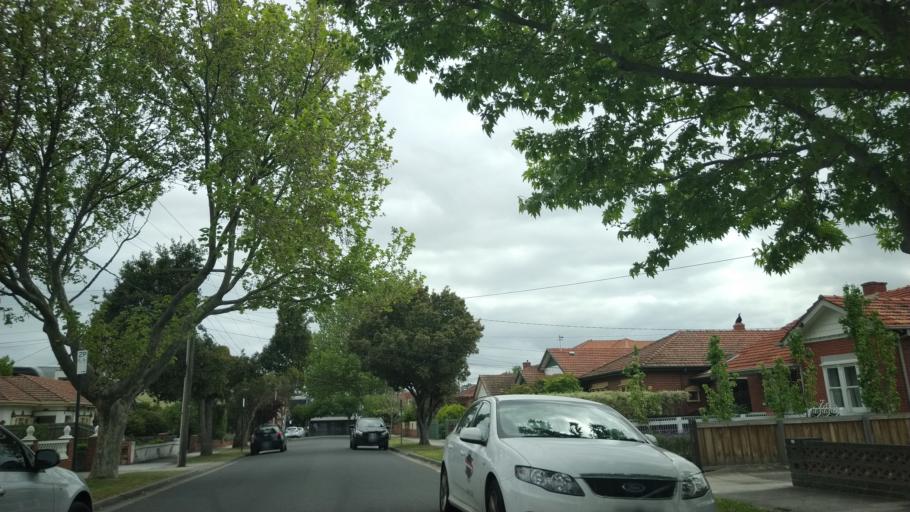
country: AU
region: Victoria
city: Hughesdale
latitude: -37.8940
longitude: 145.0789
